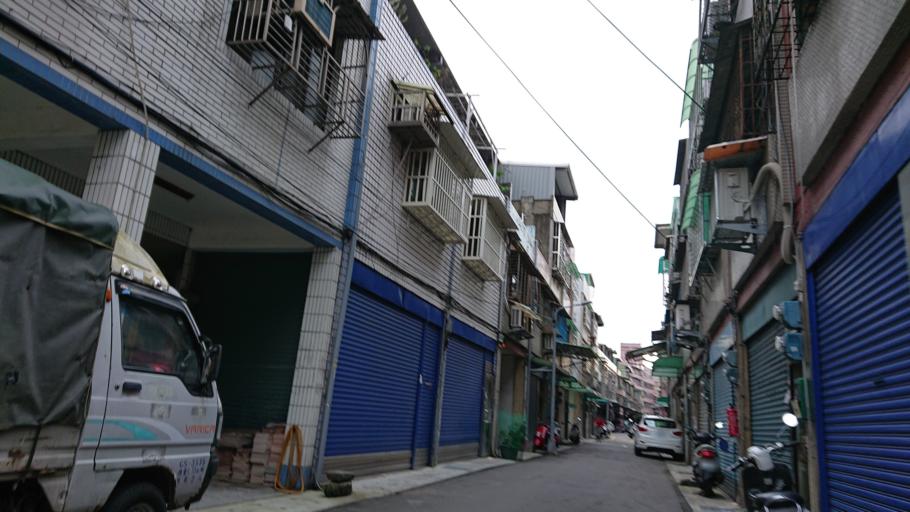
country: TW
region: Taiwan
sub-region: Taoyuan
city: Taoyuan
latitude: 24.9273
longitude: 121.3762
